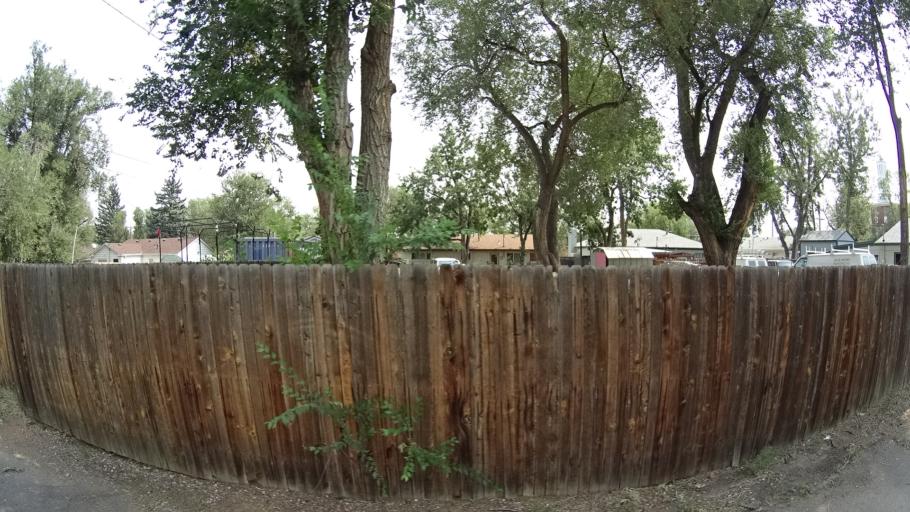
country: US
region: Colorado
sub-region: El Paso County
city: Colorado Springs
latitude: 38.8110
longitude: -104.8185
